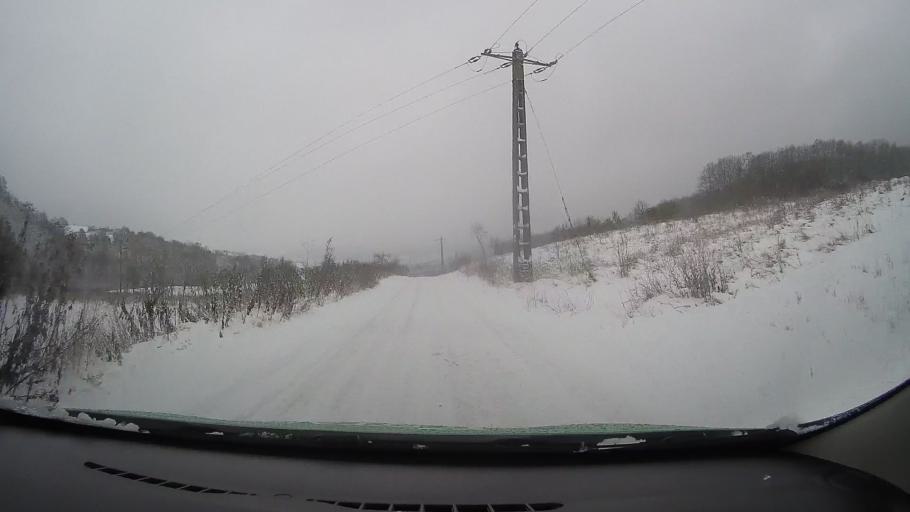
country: RO
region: Hunedoara
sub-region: Comuna Carjiti
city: Carjiti
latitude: 45.8386
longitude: 22.8366
